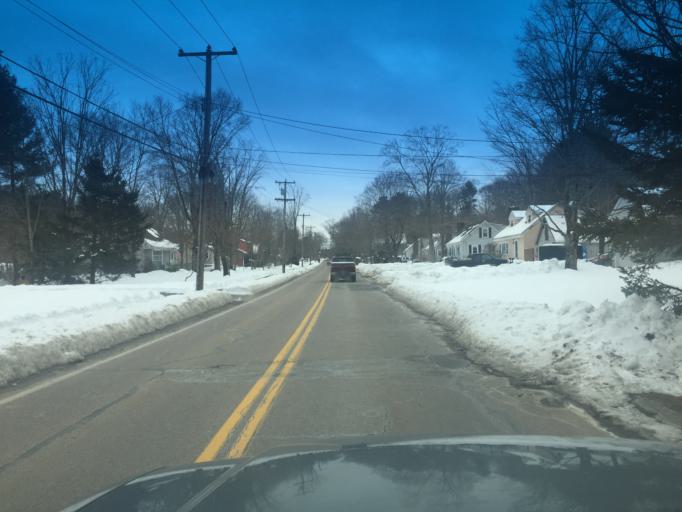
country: US
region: Massachusetts
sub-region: Norfolk County
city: Millis
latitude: 42.1612
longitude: -71.3656
